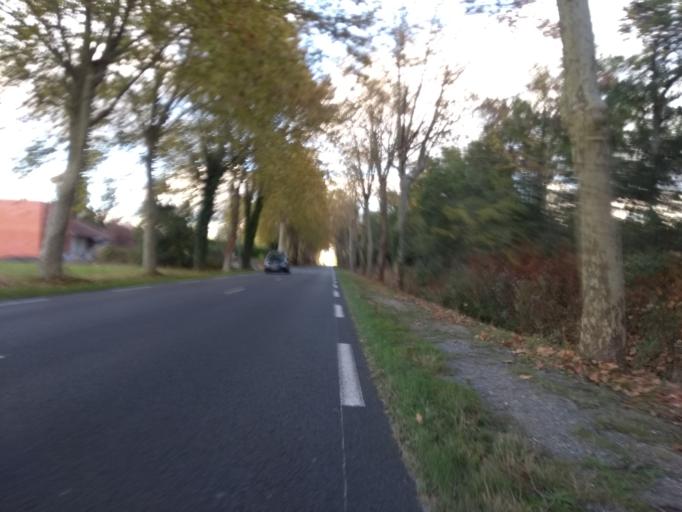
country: FR
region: Aquitaine
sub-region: Departement de la Gironde
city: Cestas
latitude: 44.7068
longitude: -0.7001
